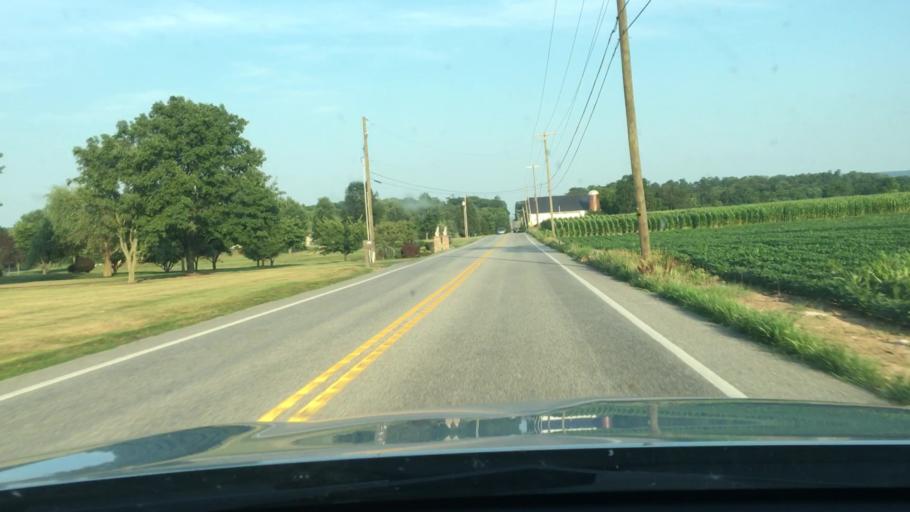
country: US
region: Pennsylvania
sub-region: Cumberland County
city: Boiling Springs
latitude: 40.1762
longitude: -77.1280
